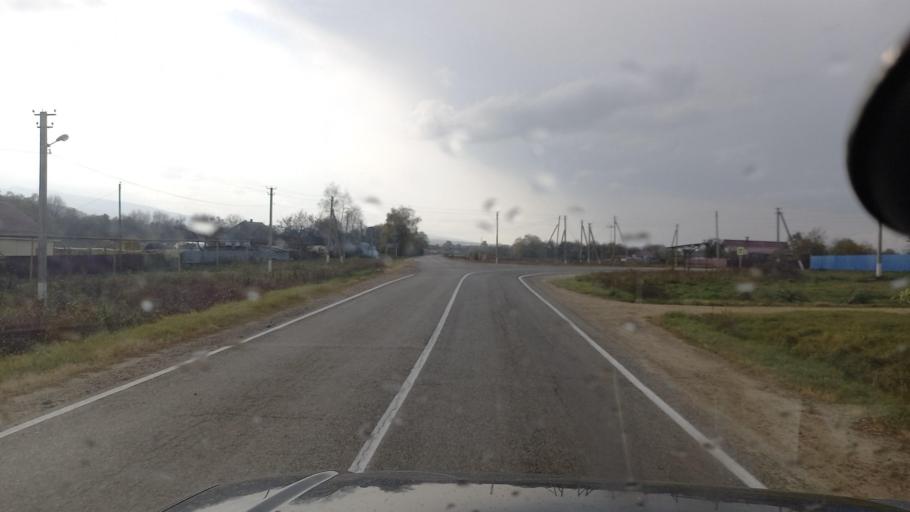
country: RU
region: Krasnodarskiy
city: Gubskaya
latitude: 44.3195
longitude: 40.6081
